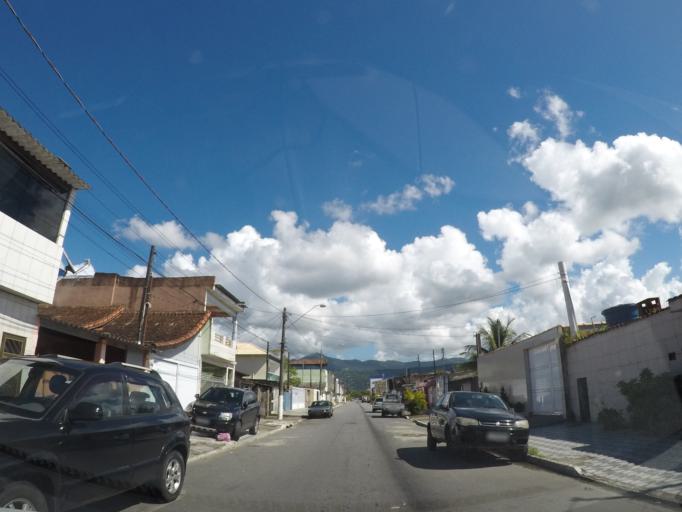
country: BR
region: Sao Paulo
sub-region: Praia Grande
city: Praia Grande
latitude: -24.0260
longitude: -46.5079
